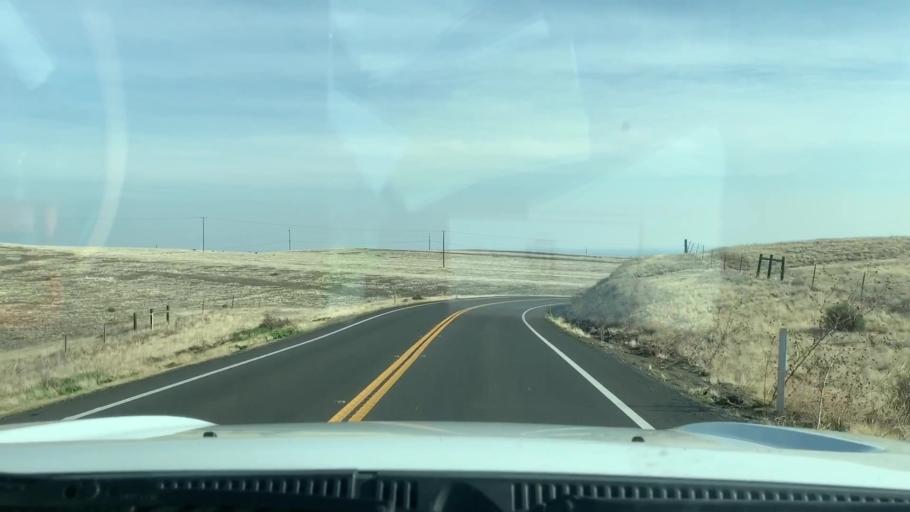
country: US
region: California
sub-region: Fresno County
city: Coalinga
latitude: 36.2492
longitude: -120.3065
